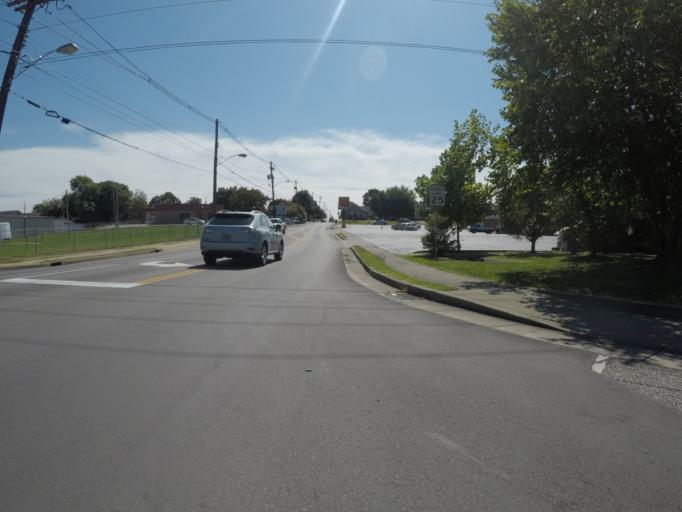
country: US
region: Kentucky
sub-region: Boyd County
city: Ashland
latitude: 38.4566
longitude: -82.6468
